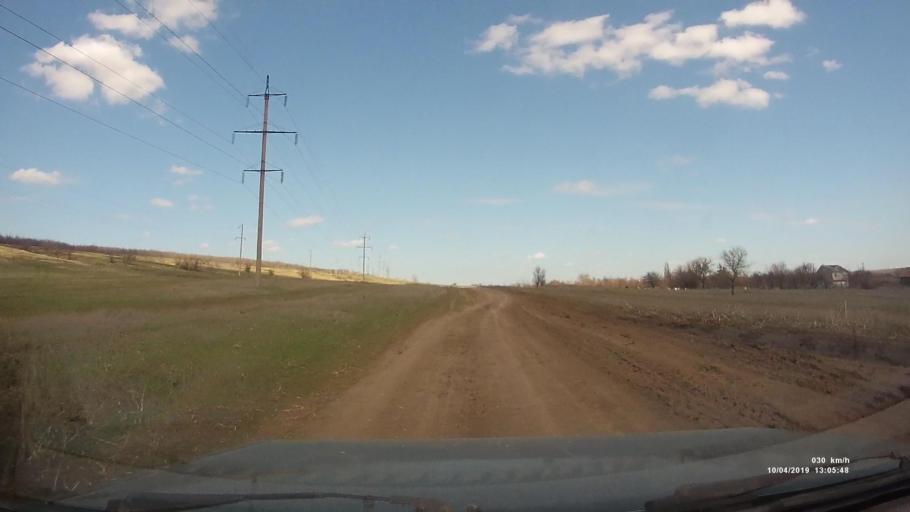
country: RU
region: Rostov
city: Masalovka
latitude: 48.3894
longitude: 40.2336
